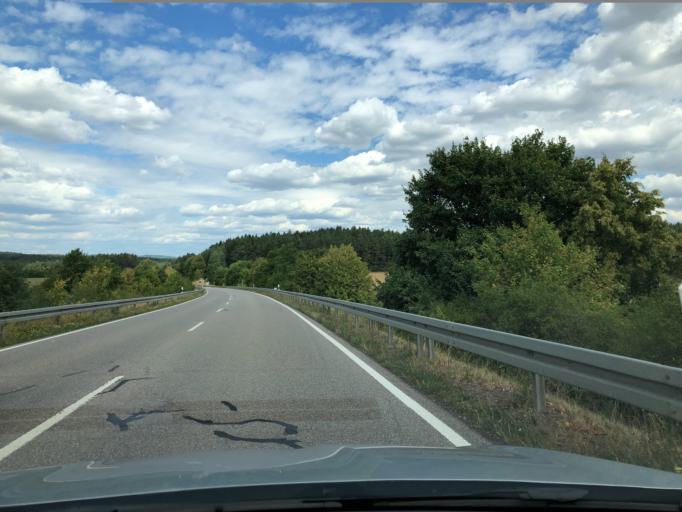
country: DE
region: Bavaria
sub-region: Upper Palatinate
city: Illschwang
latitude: 49.4687
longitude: 11.7041
